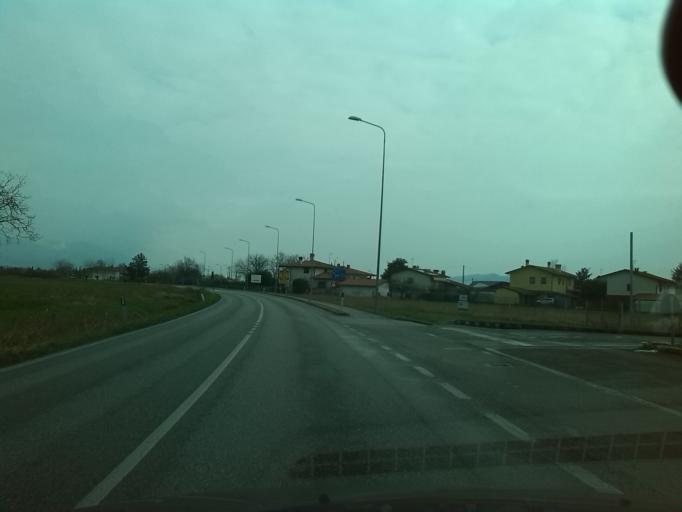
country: IT
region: Friuli Venezia Giulia
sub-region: Provincia di Gorizia
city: San Lorenzo Isontino
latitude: 45.9329
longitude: 13.5308
